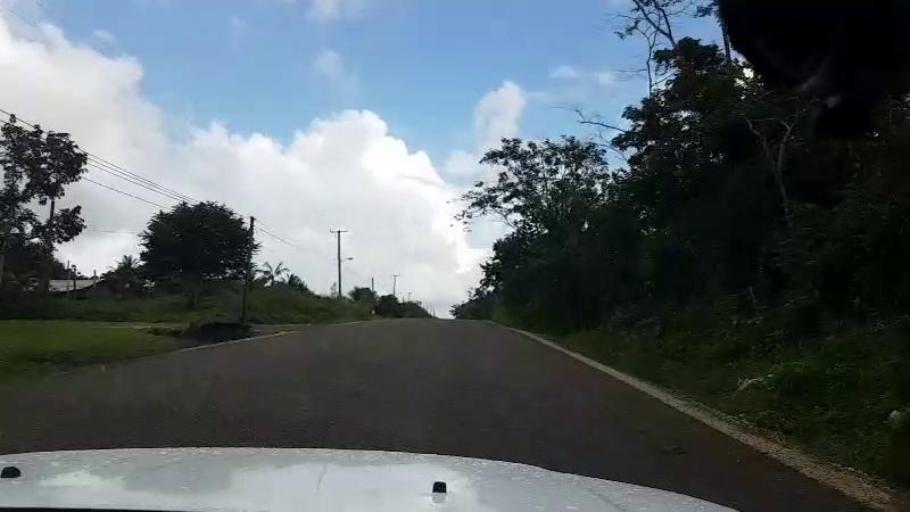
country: BZ
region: Cayo
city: Belmopan
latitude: 17.0922
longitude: -88.6424
